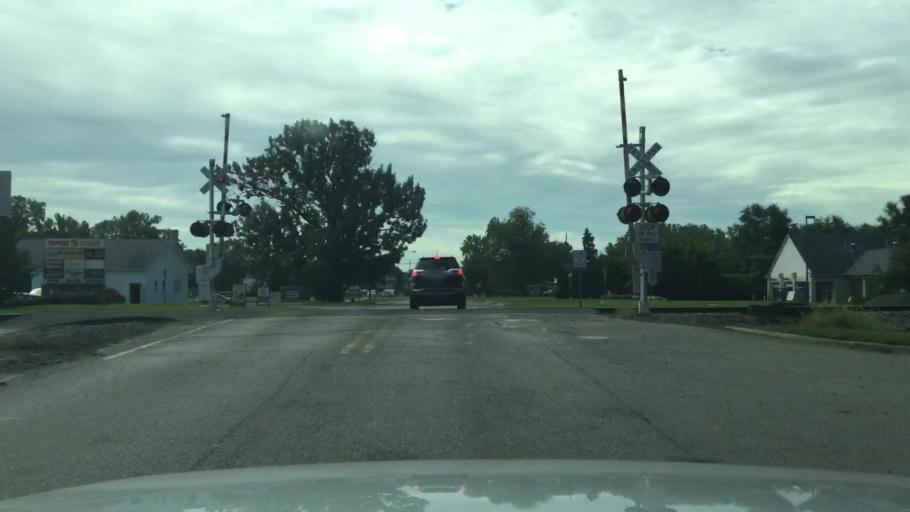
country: US
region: Michigan
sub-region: Wayne County
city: Belleville
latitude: 42.2023
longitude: -83.4852
